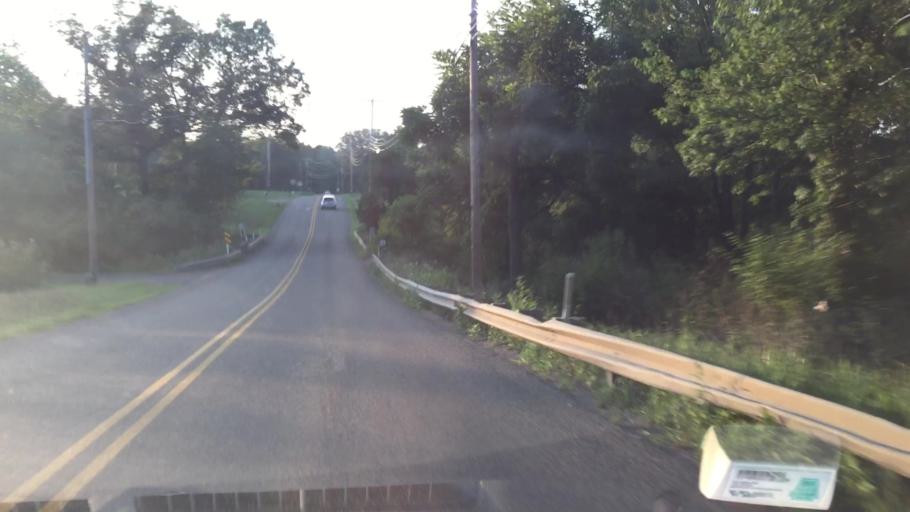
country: US
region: Pennsylvania
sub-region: Butler County
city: Seven Fields
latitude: 40.7006
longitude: -80.0488
